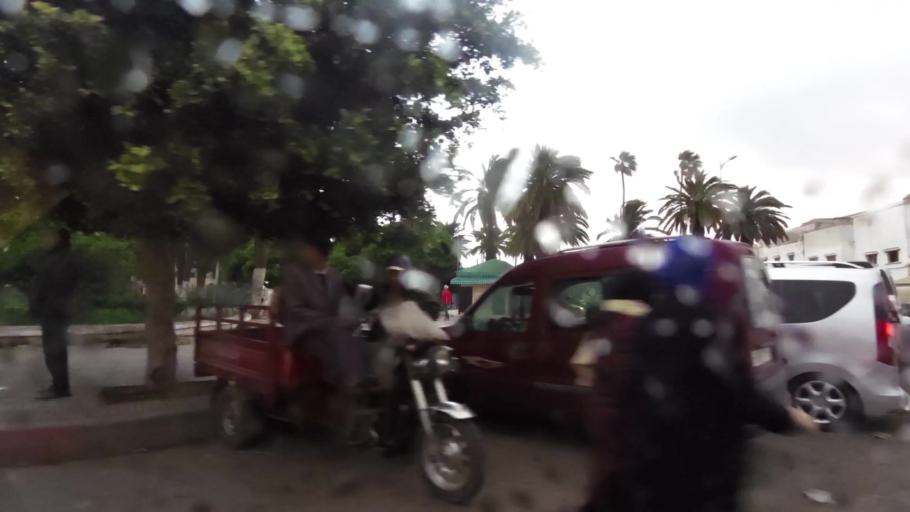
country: MA
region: Doukkala-Abda
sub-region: El-Jadida
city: El Jadida
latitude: 33.2573
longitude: -8.5055
